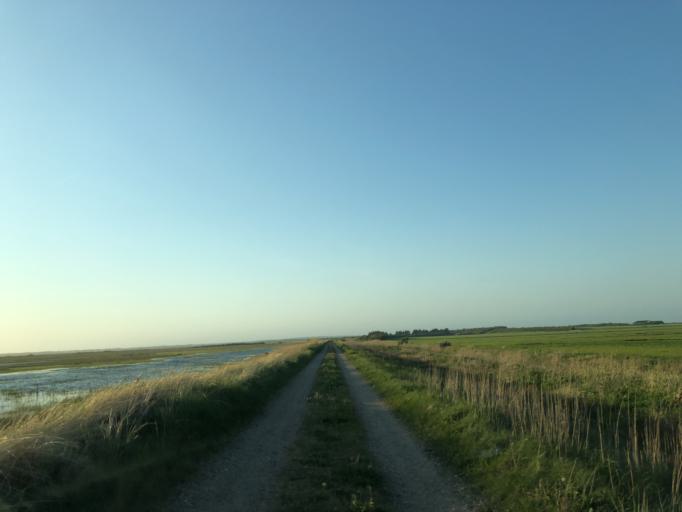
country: DK
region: Central Jutland
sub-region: Ringkobing-Skjern Kommune
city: Ringkobing
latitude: 56.2195
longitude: 8.1655
